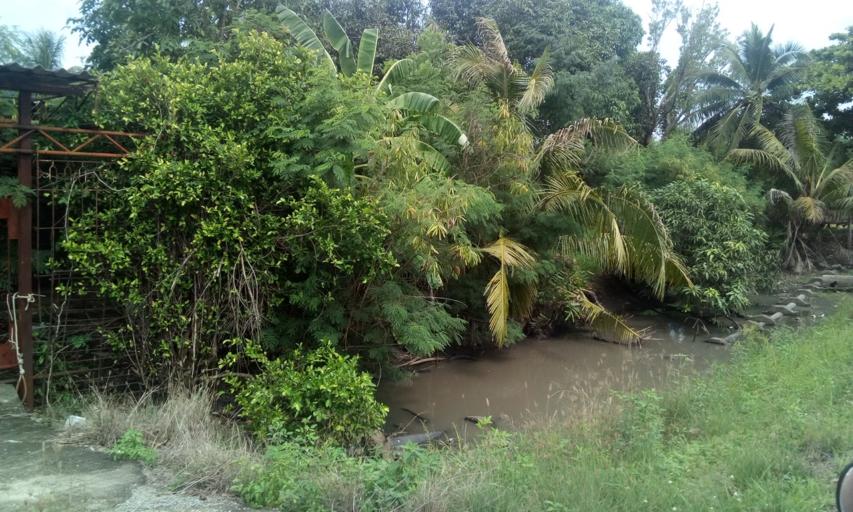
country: TH
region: Pathum Thani
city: Ban Lam Luk Ka
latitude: 14.0137
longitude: 100.8429
